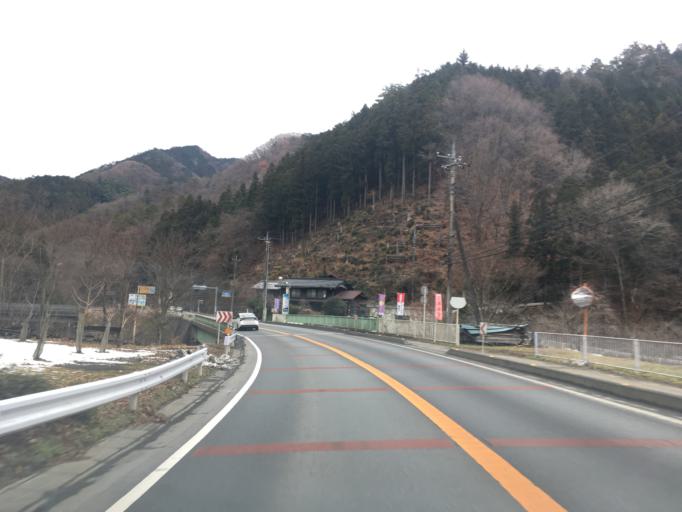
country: JP
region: Saitama
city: Chichibu
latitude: 35.9694
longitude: 139.1615
